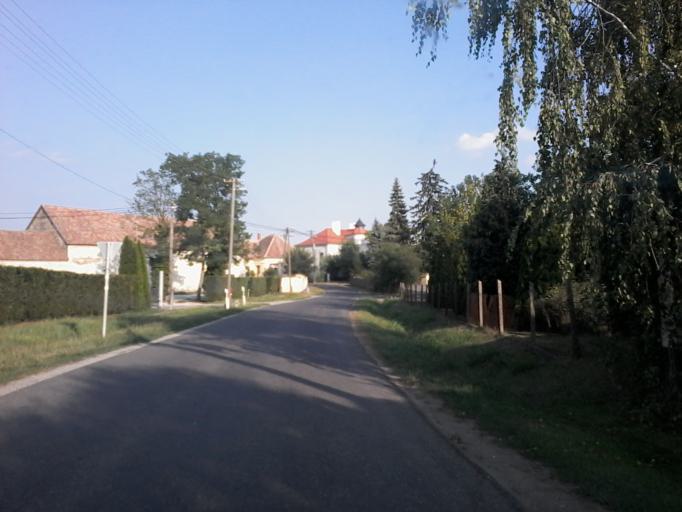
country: HU
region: Vas
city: Janoshaza
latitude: 47.1169
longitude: 17.1982
